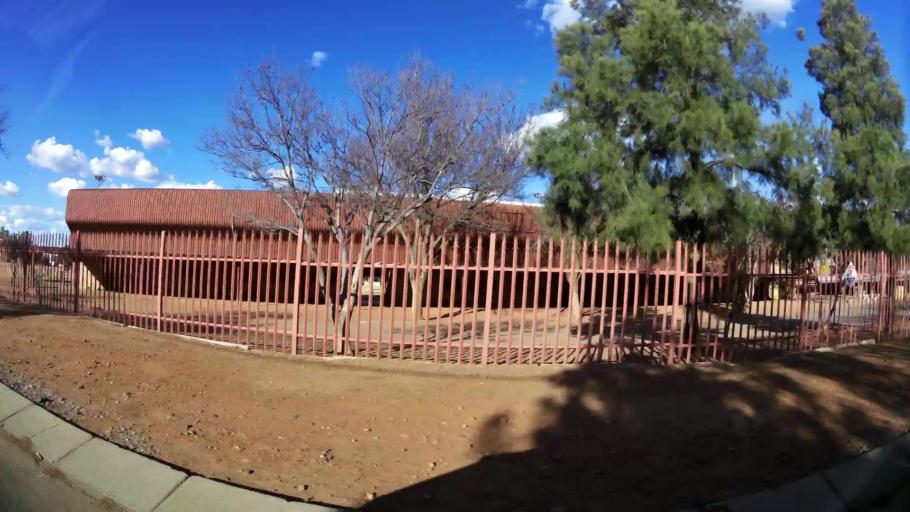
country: ZA
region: North-West
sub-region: Dr Kenneth Kaunda District Municipality
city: Klerksdorp
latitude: -26.8419
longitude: 26.6623
